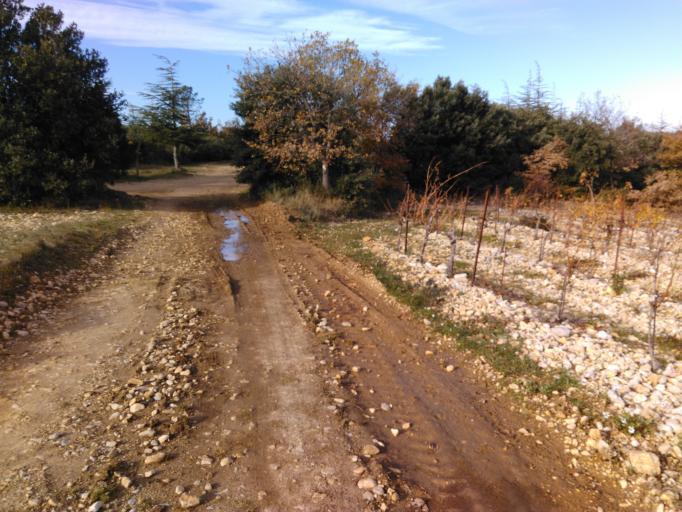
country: FR
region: Rhone-Alpes
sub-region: Departement de la Drome
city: Tulette
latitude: 44.2480
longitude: 4.9612
